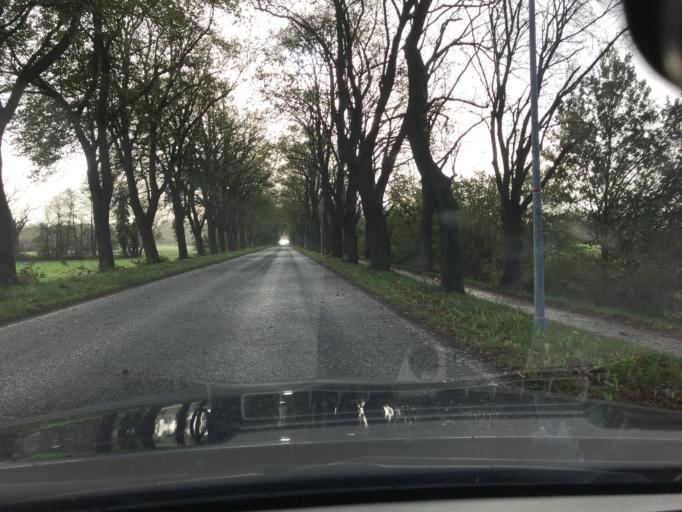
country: DE
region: Lower Saxony
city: Syke
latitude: 52.9452
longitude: 8.8197
